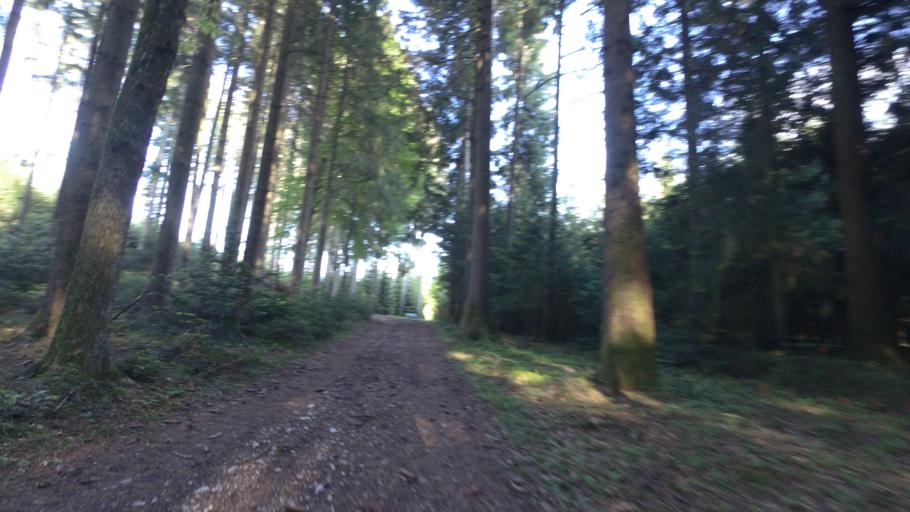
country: DE
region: Bavaria
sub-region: Upper Bavaria
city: Nussdorf
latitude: 47.8947
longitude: 12.5851
